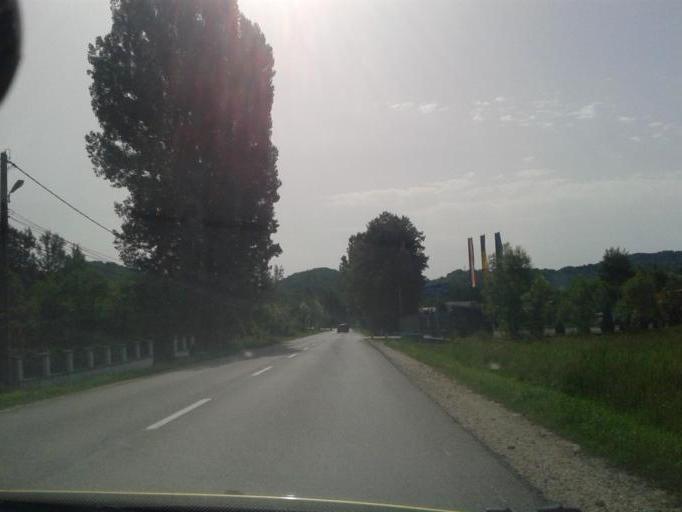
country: RO
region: Valcea
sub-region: Comuna Barbatesti
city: Bodesti
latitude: 45.1310
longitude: 24.1027
